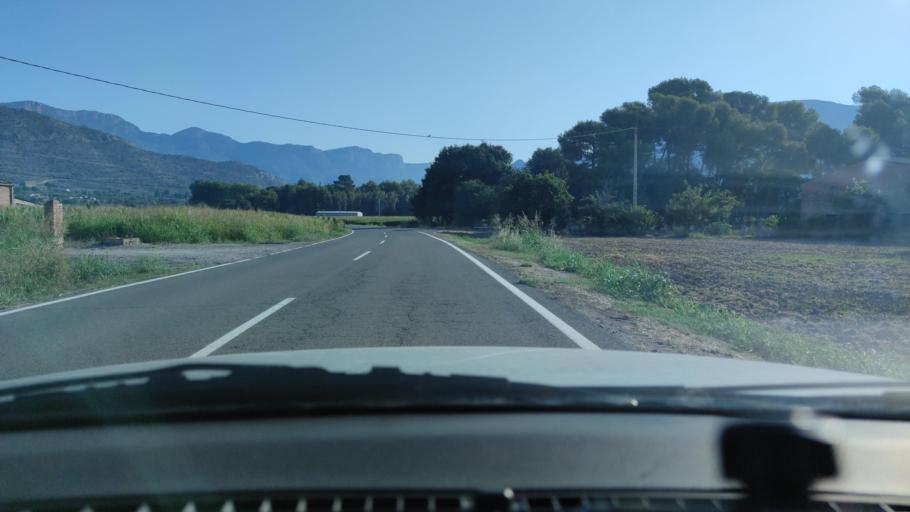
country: ES
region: Catalonia
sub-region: Provincia de Lleida
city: Camarasa
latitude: 41.8545
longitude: 0.8311
